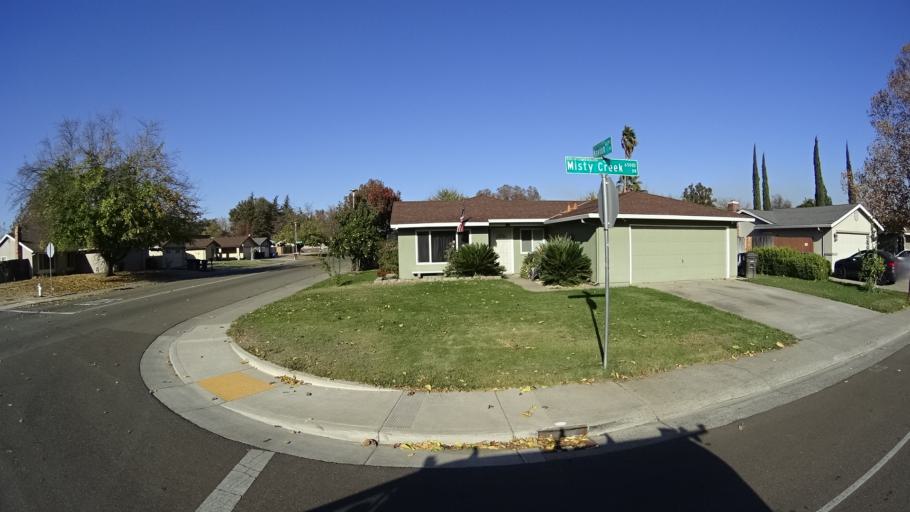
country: US
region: California
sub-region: Sacramento County
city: Antelope
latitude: 38.6992
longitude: -121.3159
